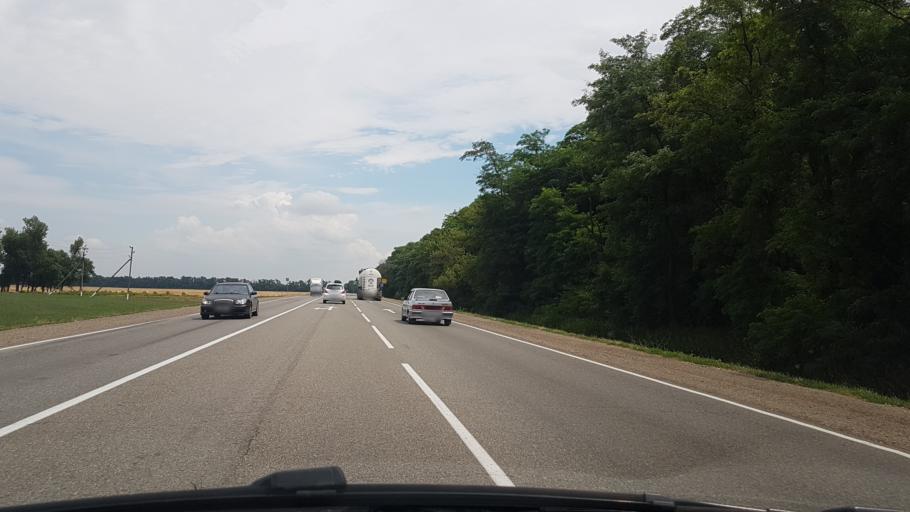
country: RU
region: Krasnodarskiy
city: Vasyurinskaya
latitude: 45.1633
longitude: 39.4660
